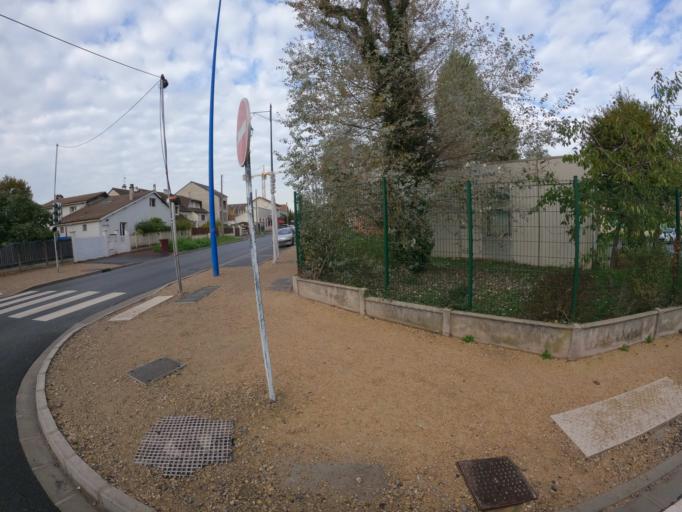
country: FR
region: Ile-de-France
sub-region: Departement de Seine-Saint-Denis
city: Montfermeil
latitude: 48.9028
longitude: 2.5938
